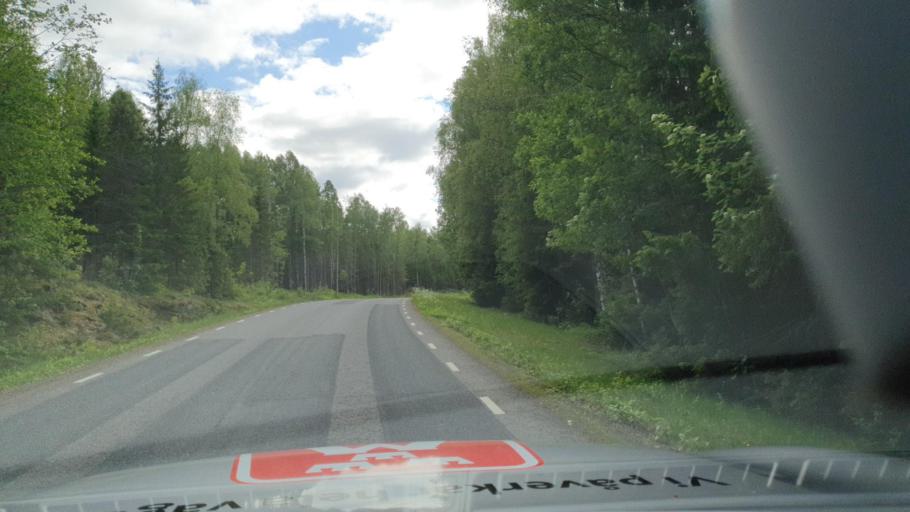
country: SE
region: Vaesternorrland
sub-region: Kramfors Kommun
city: Nordingra
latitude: 62.8095
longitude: 18.1559
